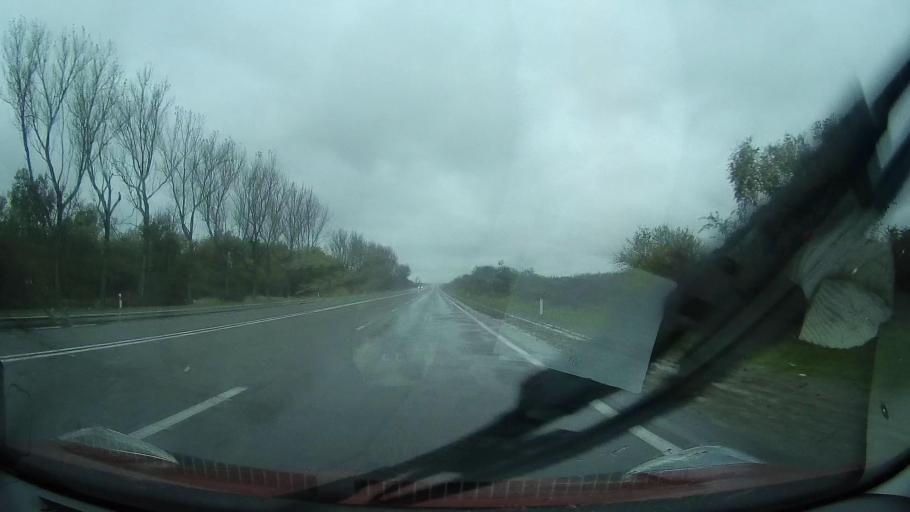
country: RU
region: Stavropol'skiy
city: Nevinnomyssk
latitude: 44.6304
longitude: 42.0299
